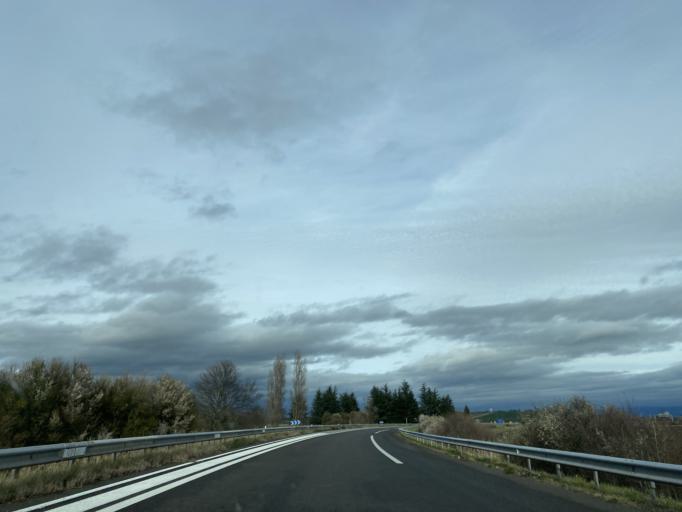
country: FR
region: Auvergne
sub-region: Departement du Puy-de-Dome
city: Pont-du-Chateau
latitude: 45.8266
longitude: 3.2263
